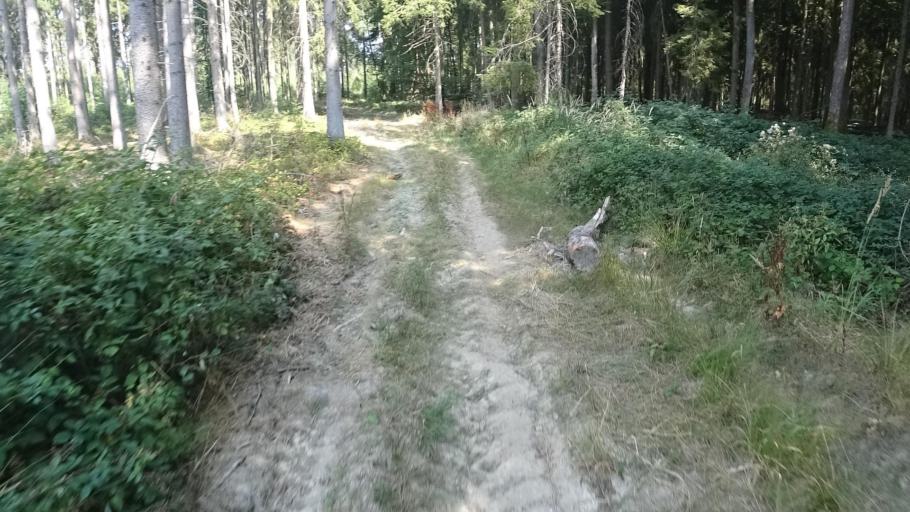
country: DE
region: Rheinland-Pfalz
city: Morschbach
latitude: 50.0014
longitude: 7.6314
